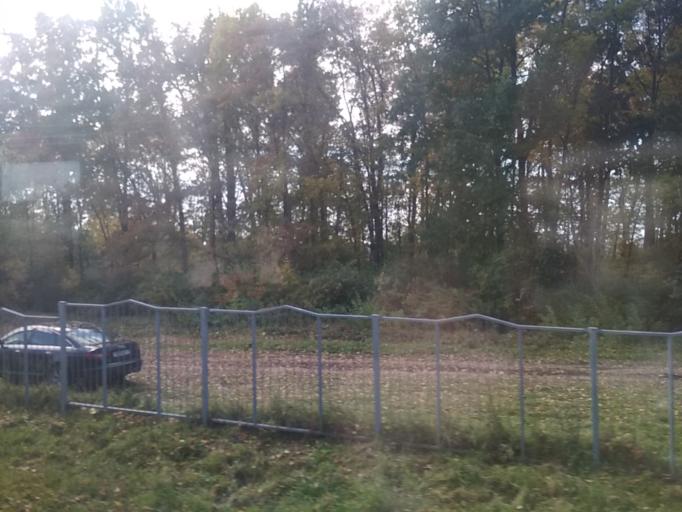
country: BY
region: Minsk
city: Syenitsa
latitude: 53.8269
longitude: 27.5678
